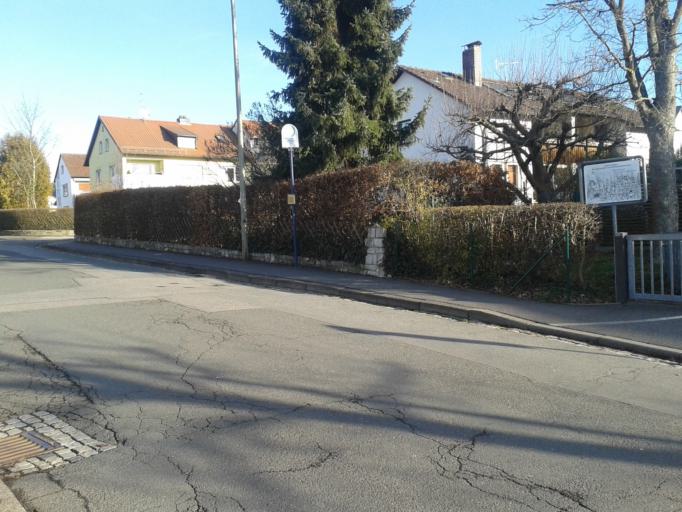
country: DE
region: Bavaria
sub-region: Upper Franconia
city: Kronach
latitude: 50.2365
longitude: 11.3371
